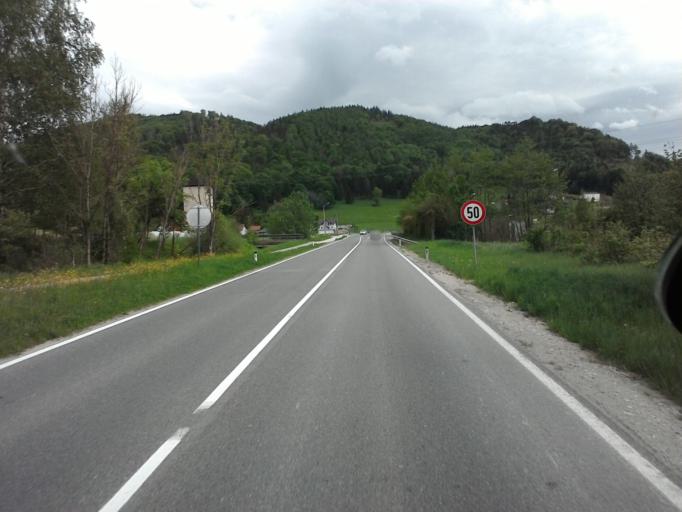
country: AT
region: Upper Austria
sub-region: Politischer Bezirk Kirchdorf an der Krems
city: Micheldorf in Oberoesterreich
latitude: 47.8637
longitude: 14.1505
